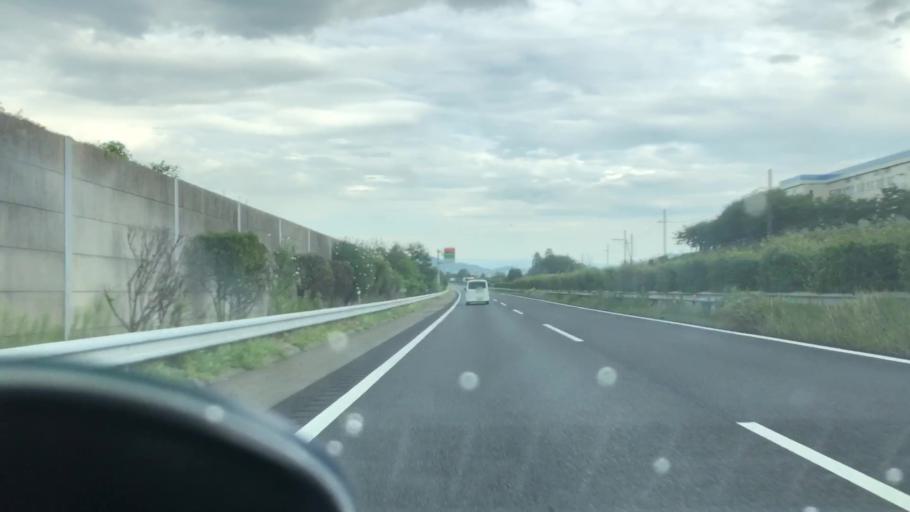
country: JP
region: Hyogo
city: Ono
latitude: 34.9451
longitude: 134.8068
